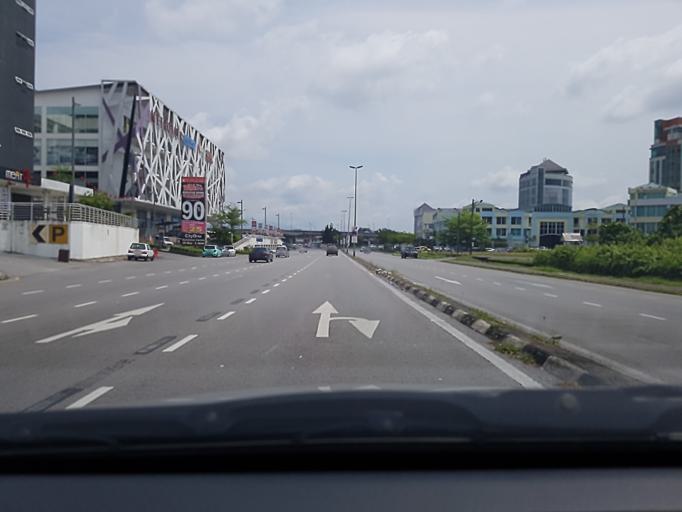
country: MY
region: Sarawak
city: Kuching
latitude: 1.5205
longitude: 110.3565
